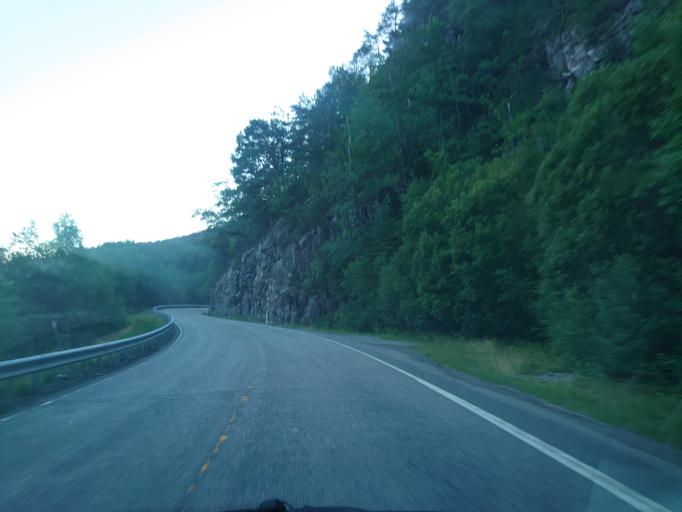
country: NO
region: Hordaland
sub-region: Osteroy
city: Lonevag
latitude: 60.6434
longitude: 5.4962
